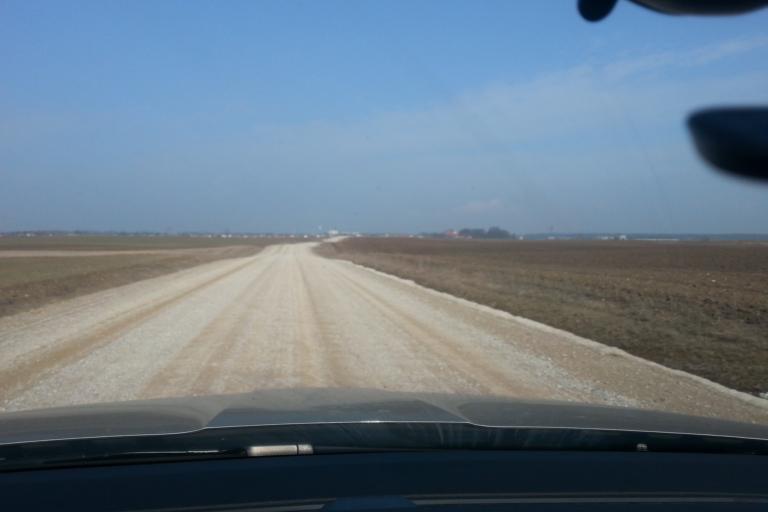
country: LT
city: Trakai
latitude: 54.5934
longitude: 24.9776
